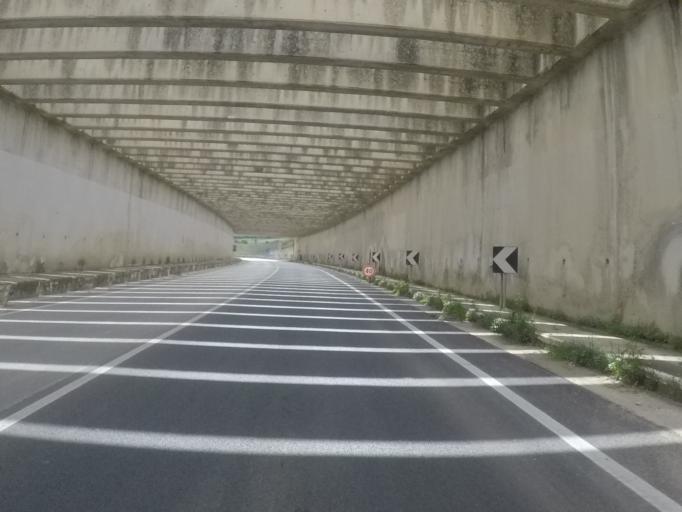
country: IT
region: Sicily
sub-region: Enna
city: Pietraperzia
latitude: 37.4151
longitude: 14.1220
